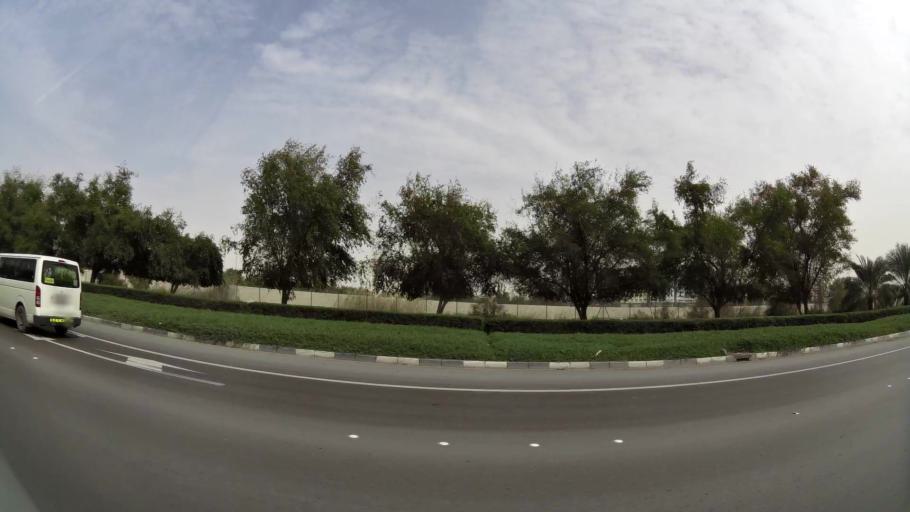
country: AE
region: Abu Dhabi
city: Abu Dhabi
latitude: 24.3454
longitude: 54.5264
